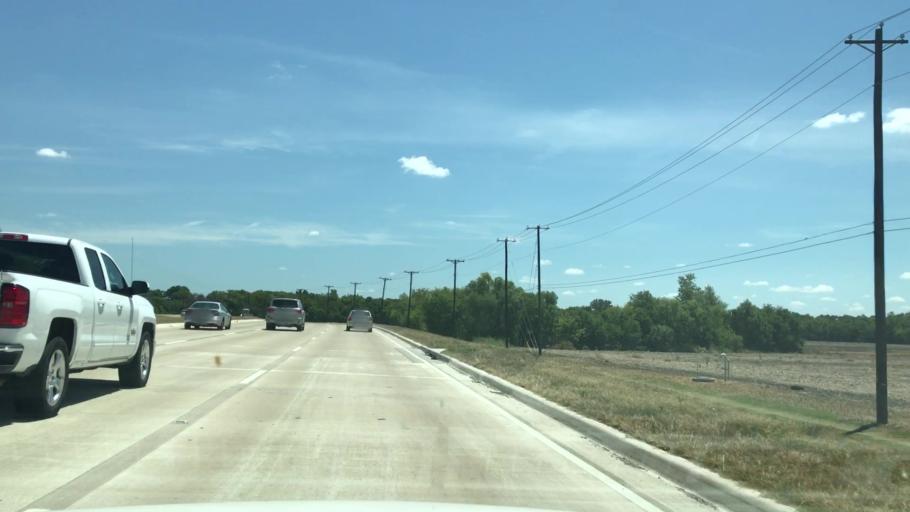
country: US
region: Texas
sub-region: Collin County
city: Lavon
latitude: 33.0222
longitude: -96.4724
